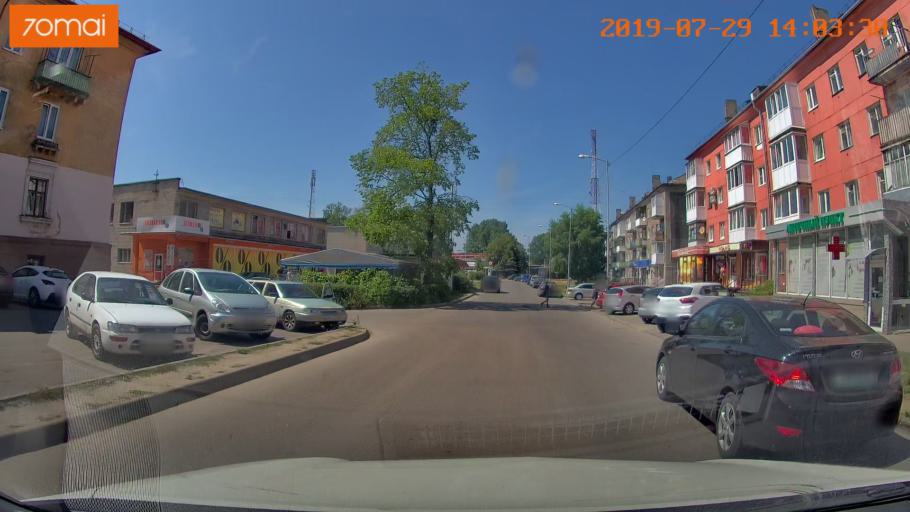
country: RU
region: Kaliningrad
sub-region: Gorod Kaliningrad
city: Baltiysk
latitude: 54.6590
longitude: 19.9131
